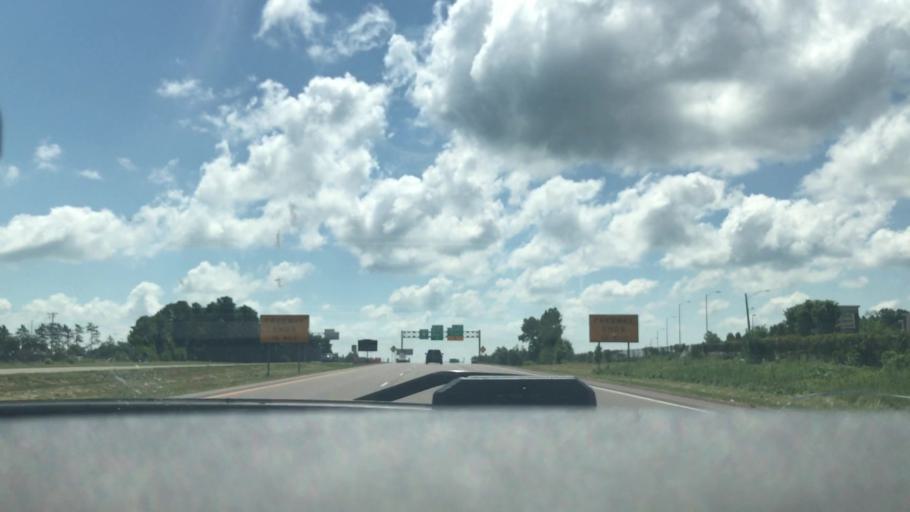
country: US
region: Wisconsin
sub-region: Eau Claire County
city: Altoona
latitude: 44.7748
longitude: -91.4316
